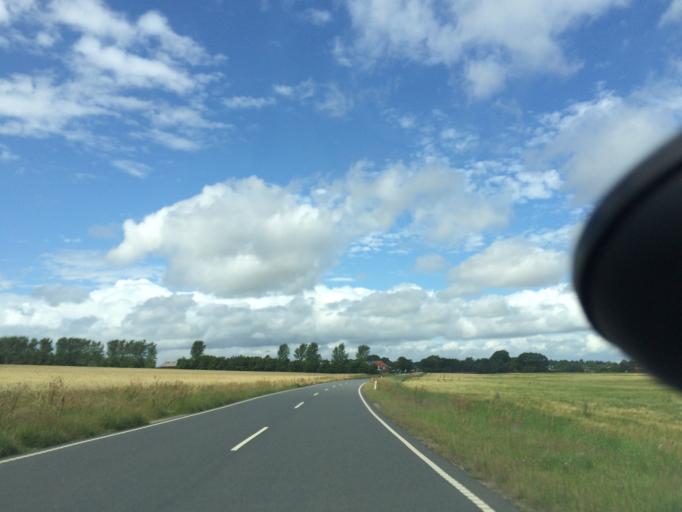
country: DK
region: Central Jutland
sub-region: Silkeborg Kommune
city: Svejbaek
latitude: 56.1864
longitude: 9.7074
